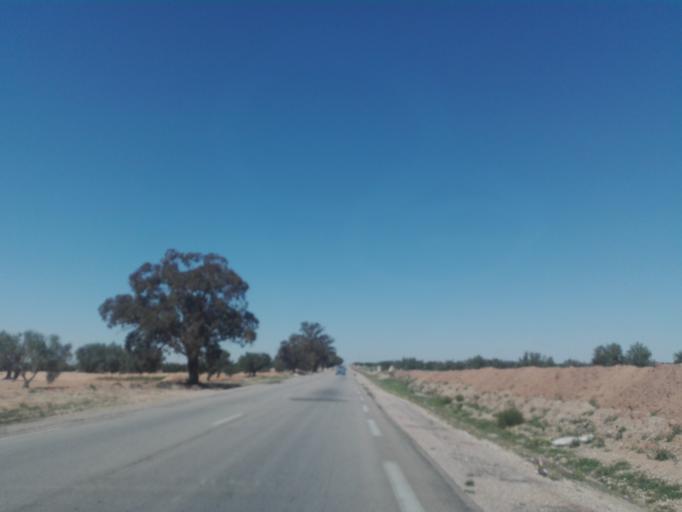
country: TN
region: Safaqis
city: Bi'r `Ali Bin Khalifah
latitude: 34.7575
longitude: 10.3174
